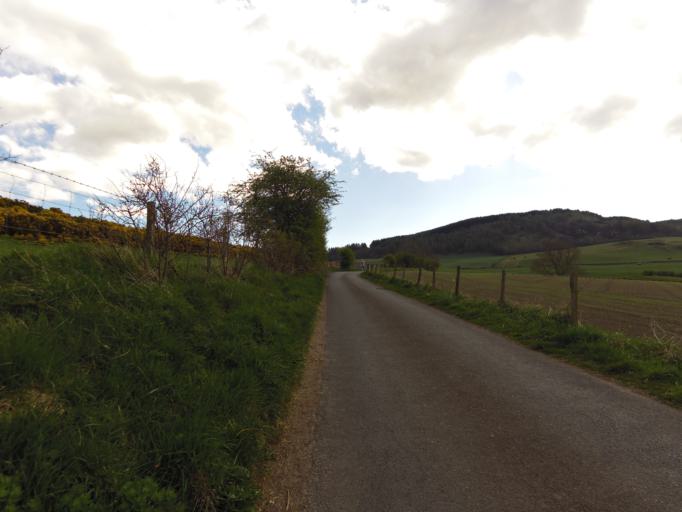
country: GB
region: Scotland
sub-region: Fife
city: Newburgh
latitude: 56.3407
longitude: -3.2526
